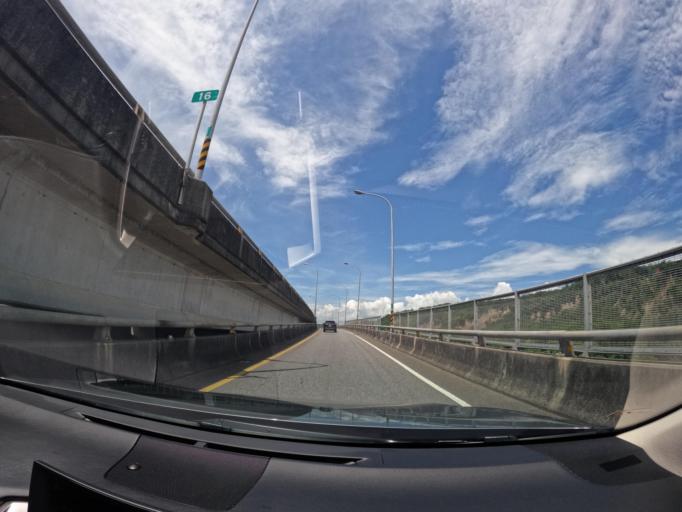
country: TW
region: Taiwan
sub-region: Miaoli
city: Miaoli
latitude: 24.5328
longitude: 120.8147
